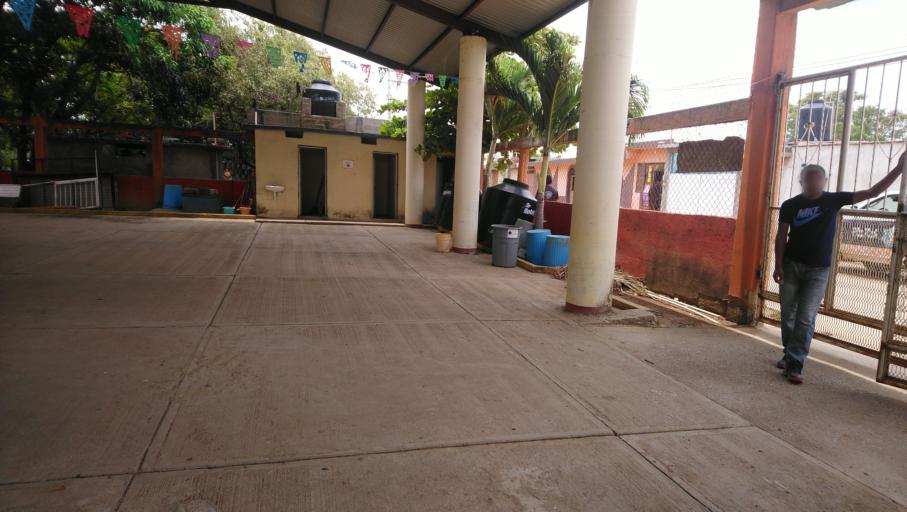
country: MX
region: Oaxaca
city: El Espinal
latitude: 16.5564
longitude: -94.9464
